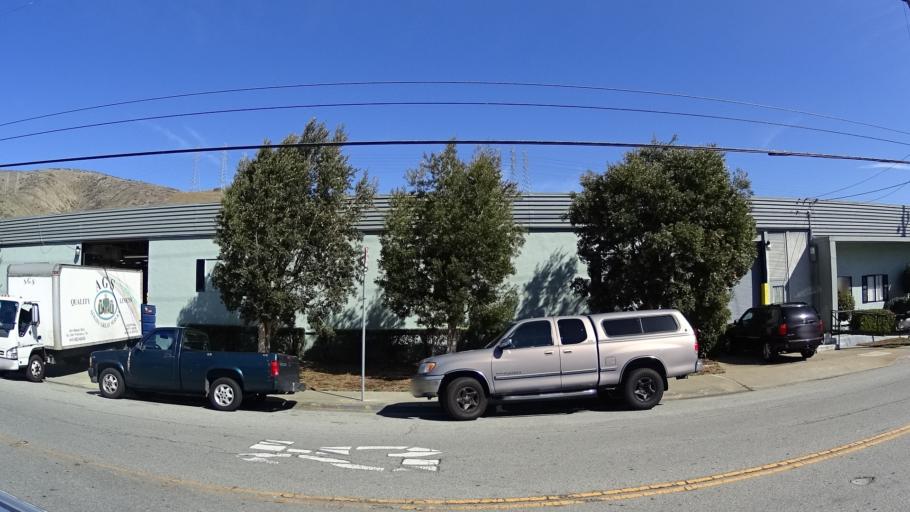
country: US
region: California
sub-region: San Mateo County
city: South San Francisco
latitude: 37.6624
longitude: -122.4077
